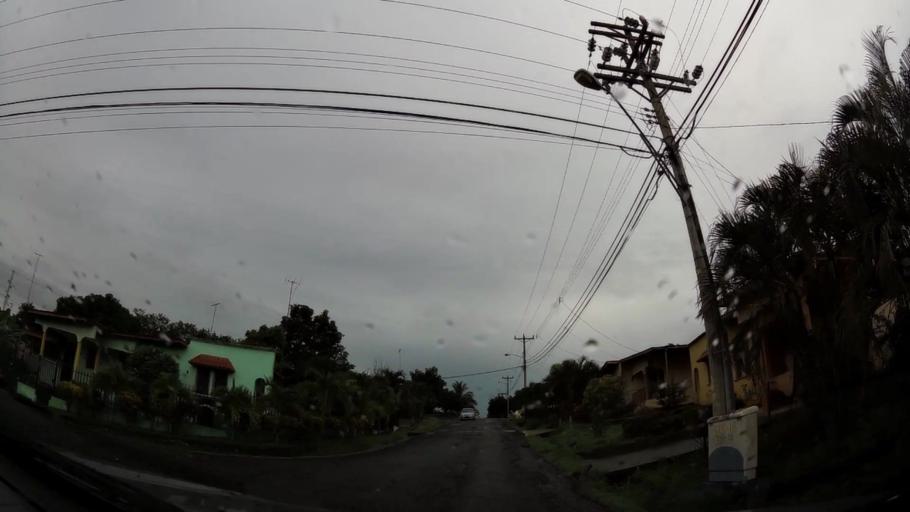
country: PA
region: Veraguas
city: Santiago de Veraguas
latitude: 8.0898
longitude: -80.9894
